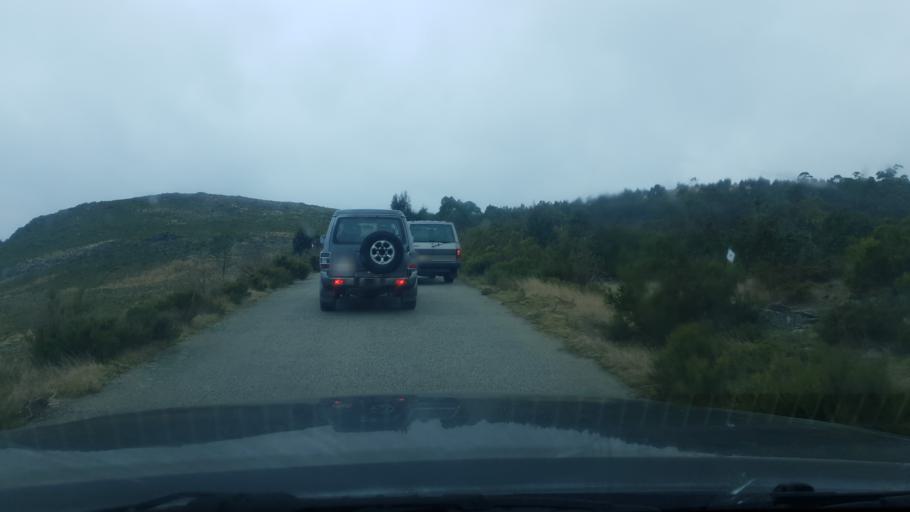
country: PT
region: Viseu
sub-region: Sao Pedro do Sul
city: Sao Pedro do Sul
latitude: 40.8553
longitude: -8.1002
